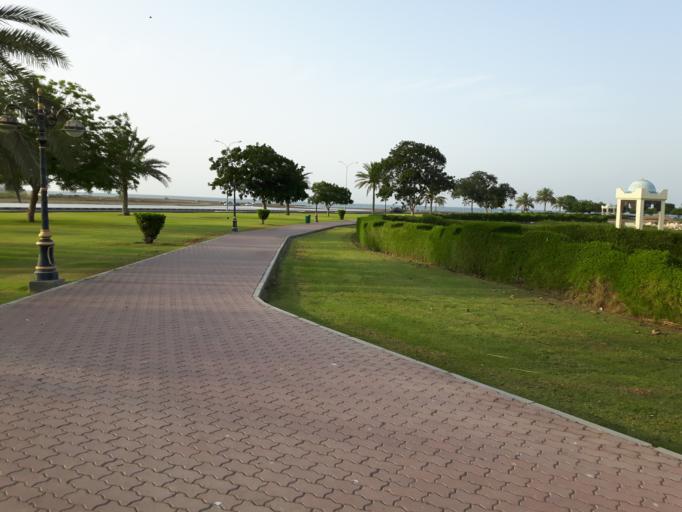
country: OM
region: Al Batinah
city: Al Sohar
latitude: 24.4064
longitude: 56.7156
